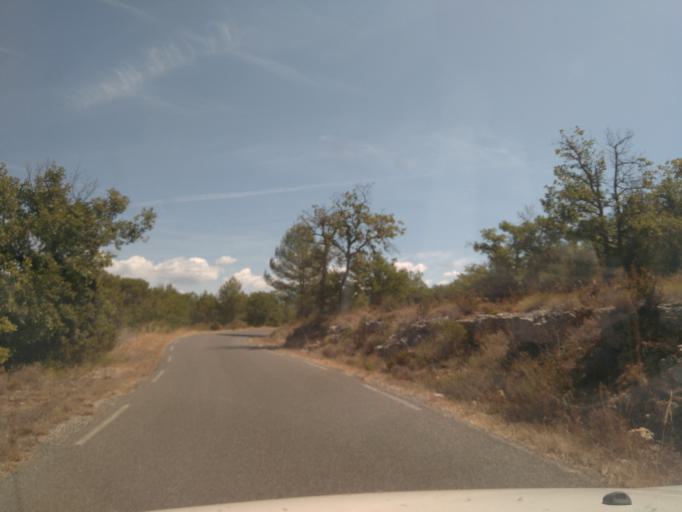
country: FR
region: Provence-Alpes-Cote d'Azur
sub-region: Departement du Var
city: Regusse
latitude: 43.7106
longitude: 6.0847
